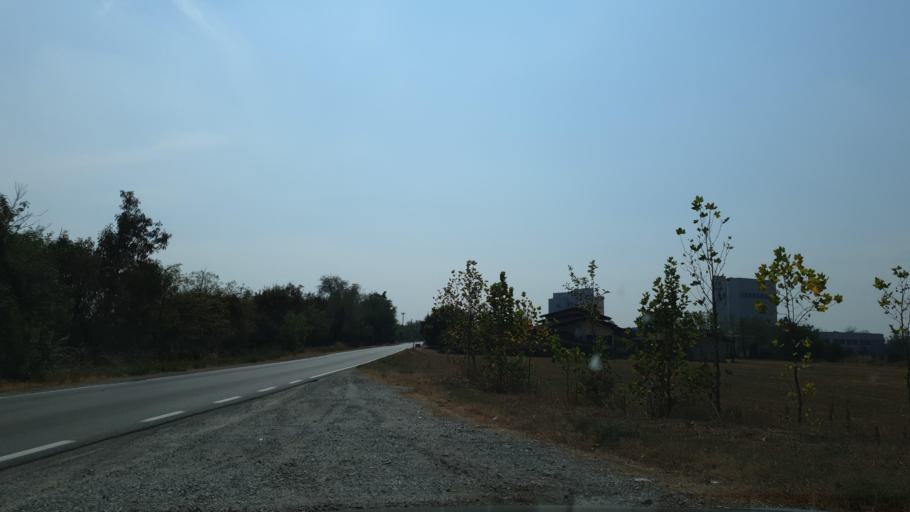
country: IT
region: Lombardy
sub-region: Provincia di Brescia
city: Montirone
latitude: 45.4356
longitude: 10.2575
